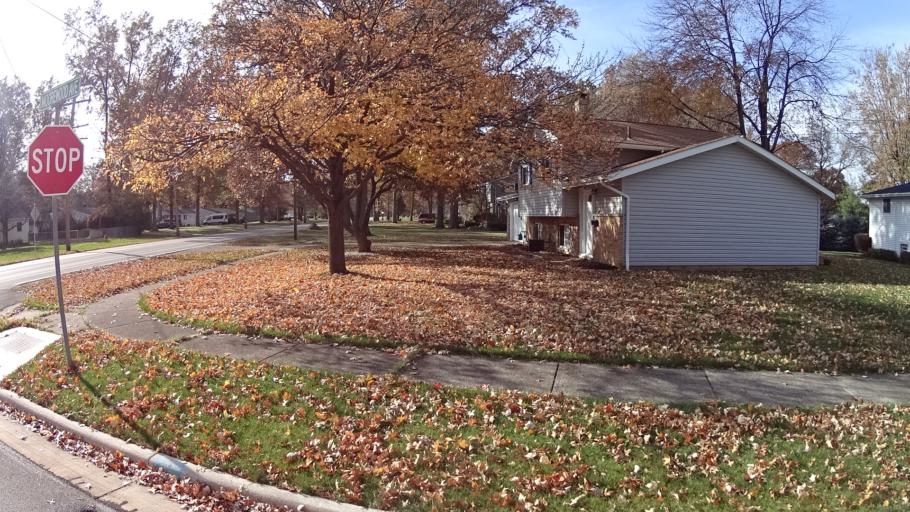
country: US
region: Ohio
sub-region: Lorain County
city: Avon Lake
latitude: 41.5090
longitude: -82.0299
